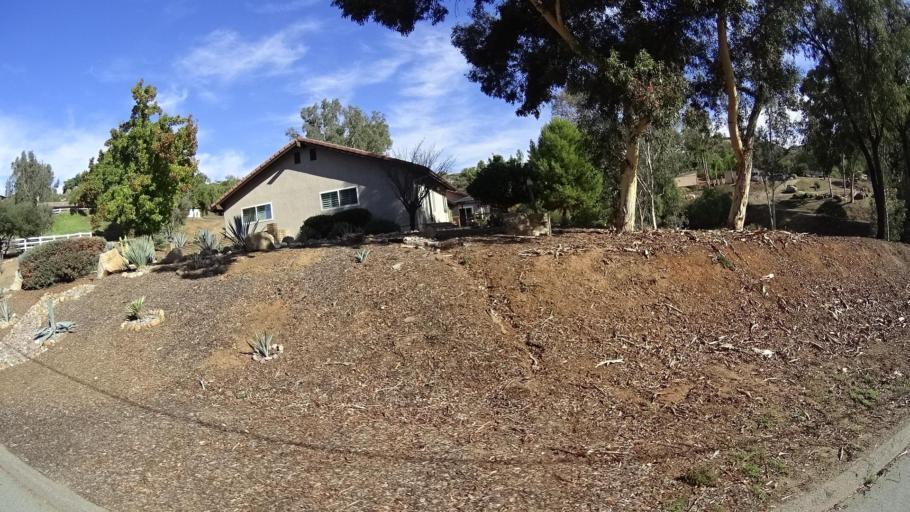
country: US
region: California
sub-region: San Diego County
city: Alpine
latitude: 32.8176
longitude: -116.7433
